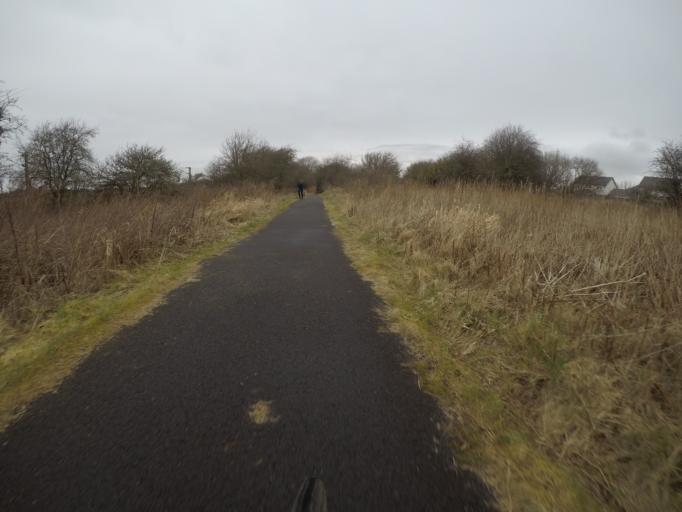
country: GB
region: Scotland
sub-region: North Ayrshire
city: Kilwinning
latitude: 55.6295
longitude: -4.6881
